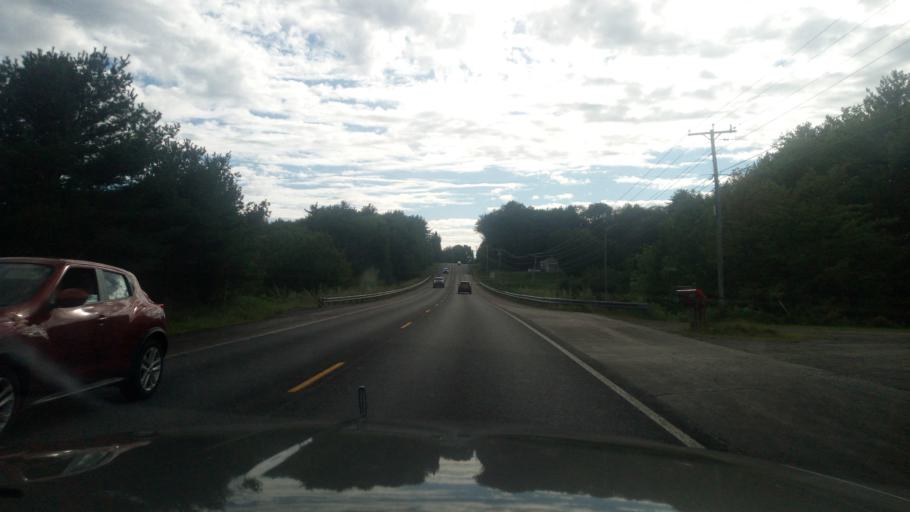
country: US
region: Maine
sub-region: Kennebec County
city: Gardiner
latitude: 44.2144
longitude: -69.8052
